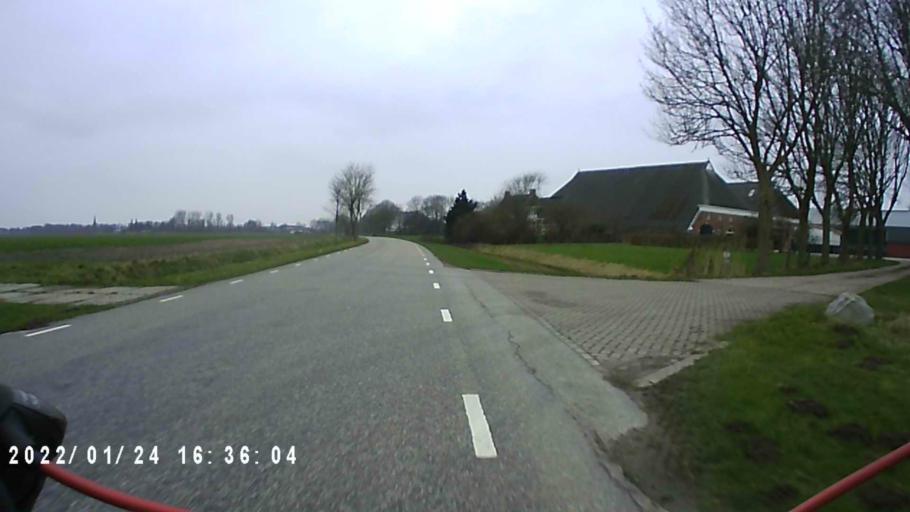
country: NL
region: Groningen
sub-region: Gemeente Zuidhorn
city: Oldehove
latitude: 53.3829
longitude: 6.4153
